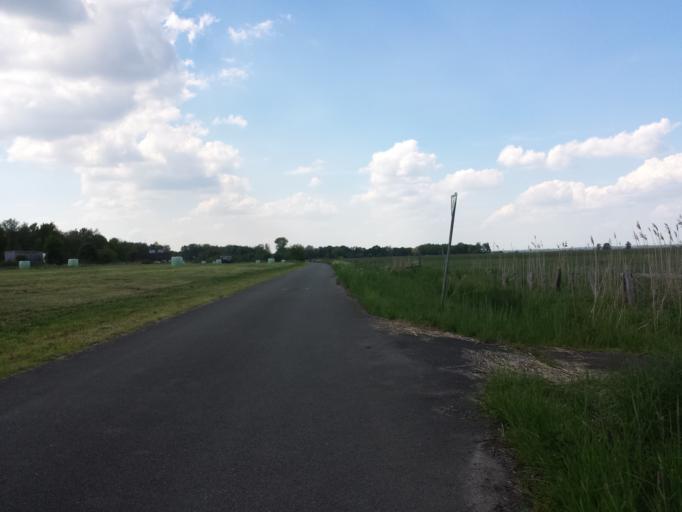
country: DE
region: Lower Saxony
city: Lilienthal
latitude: 53.1128
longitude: 8.8633
